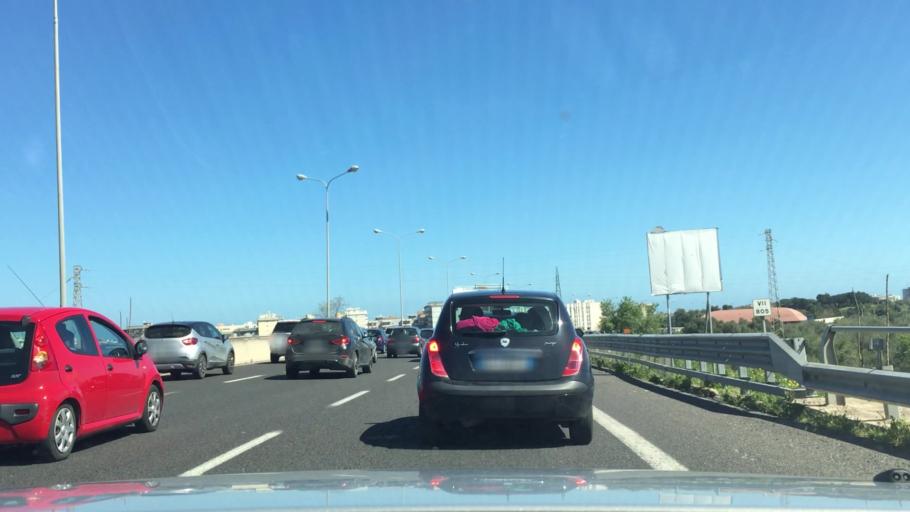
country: IT
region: Apulia
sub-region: Provincia di Bari
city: Triggiano
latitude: 41.0948
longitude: 16.8974
